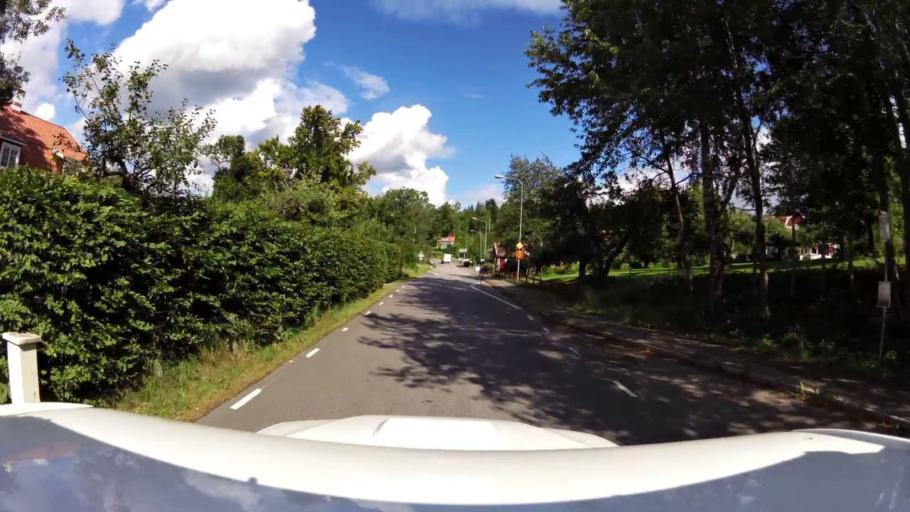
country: SE
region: OEstergoetland
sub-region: Kinda Kommun
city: Rimforsa
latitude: 58.2165
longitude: 15.6787
